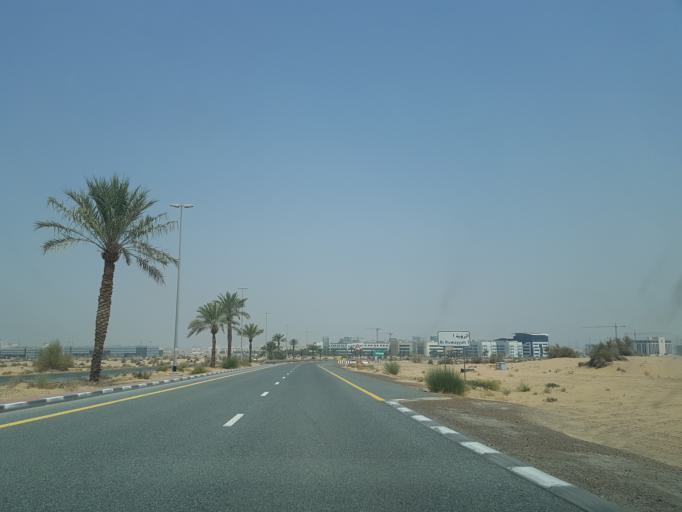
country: AE
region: Ash Shariqah
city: Sharjah
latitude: 25.1177
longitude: 55.4290
